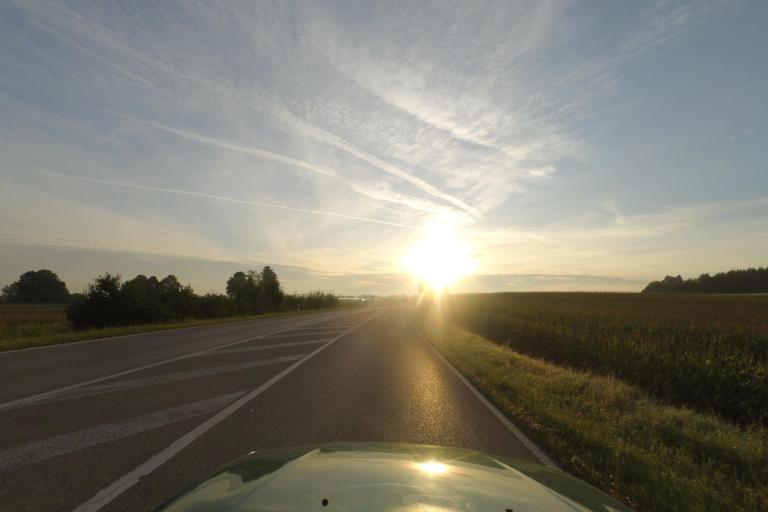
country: DE
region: Bavaria
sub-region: Upper Bavaria
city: Geltendorf
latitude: 48.1211
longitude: 10.9926
